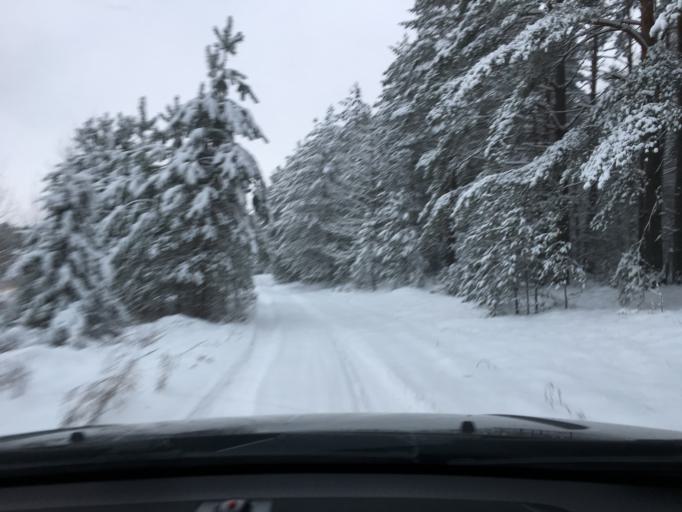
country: LT
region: Alytaus apskritis
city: Druskininkai
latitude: 53.9187
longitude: 24.1943
